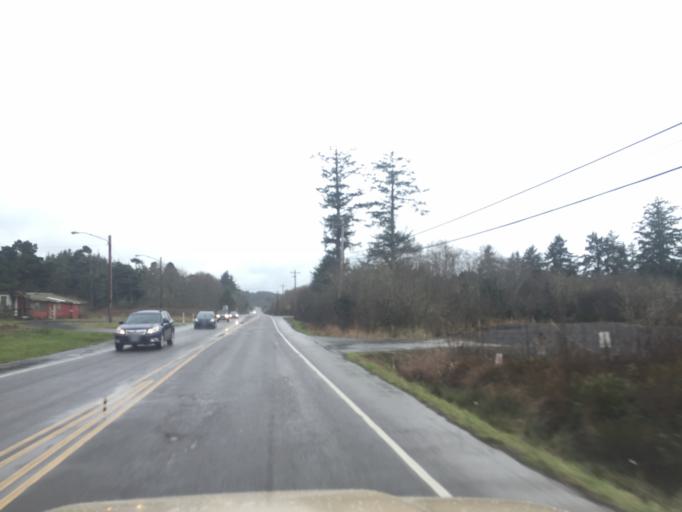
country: US
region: Oregon
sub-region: Lincoln County
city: Newport
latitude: 44.6014
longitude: -124.0574
